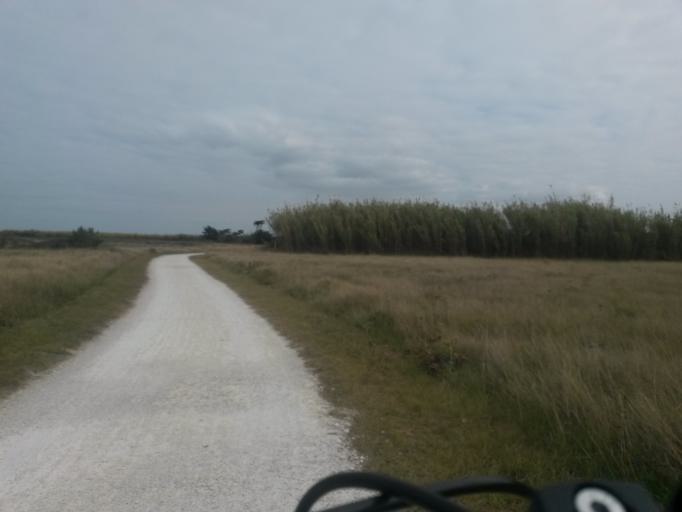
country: FR
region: Poitou-Charentes
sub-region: Departement de la Charente-Maritime
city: Saint-Denis-d'Oleron
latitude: 46.0257
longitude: -1.4021
